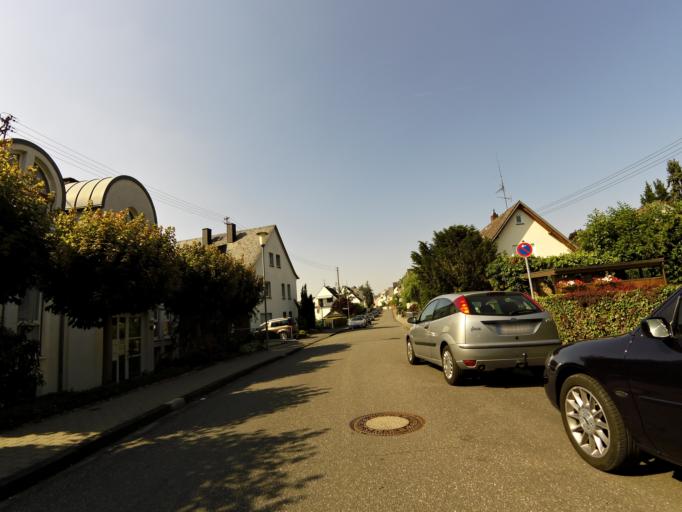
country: DE
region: Rheinland-Pfalz
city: Koblenz
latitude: 50.3410
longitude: 7.6034
